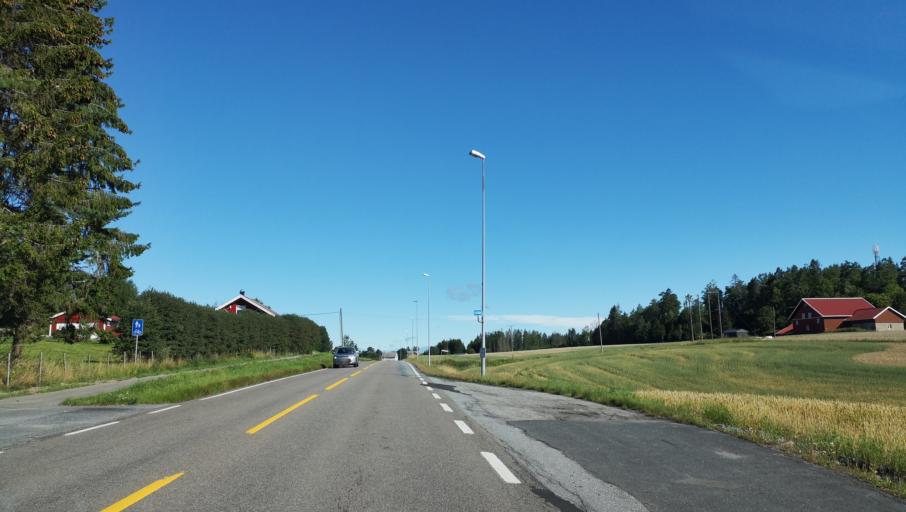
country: NO
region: Ostfold
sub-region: Spydeberg
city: Spydeberg
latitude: 59.5923
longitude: 11.1102
